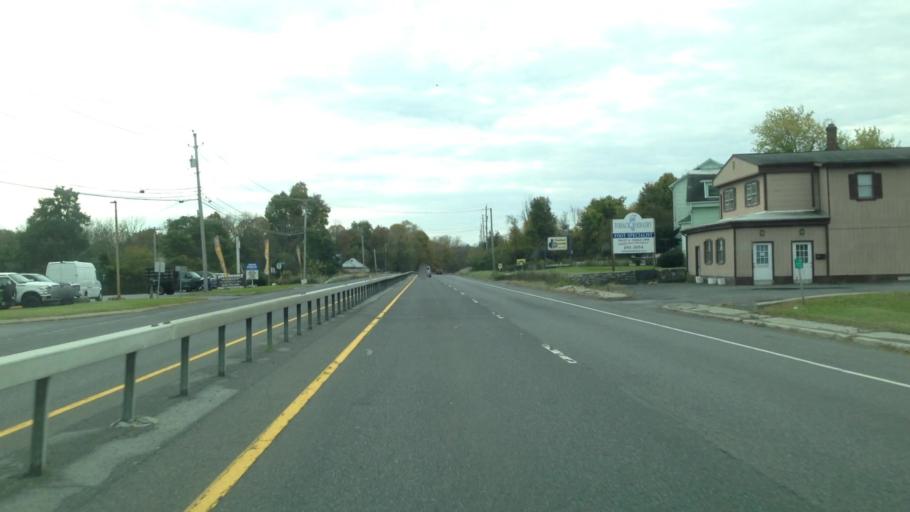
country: US
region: New York
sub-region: Ulster County
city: Highland
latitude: 41.7382
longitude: -73.9626
